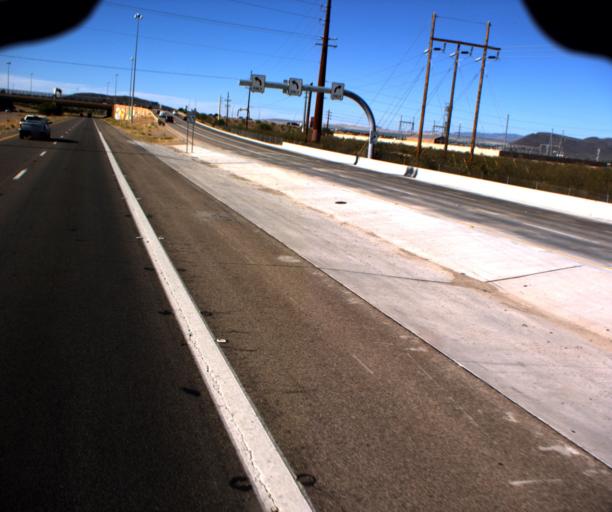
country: US
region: Arizona
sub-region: Pima County
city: Drexel Heights
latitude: 32.1375
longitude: -110.9867
